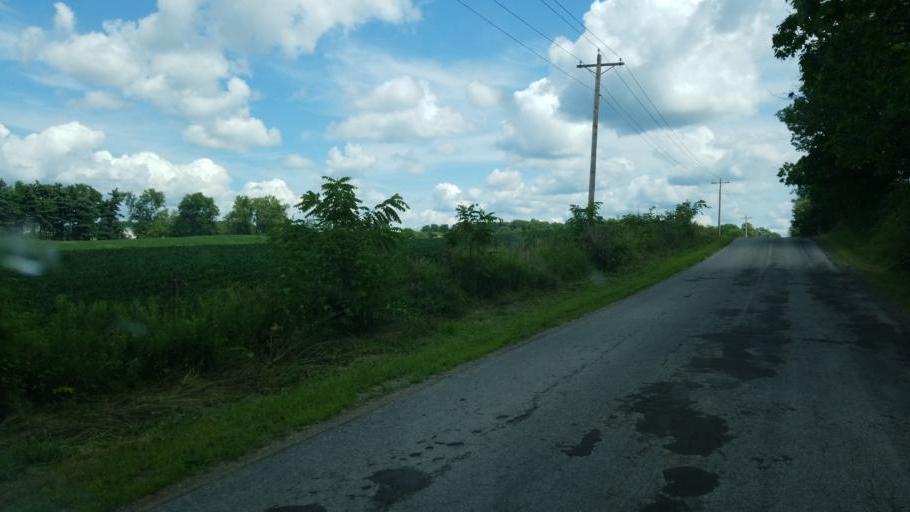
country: US
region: Ohio
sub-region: Knox County
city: Centerburg
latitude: 40.3644
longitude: -82.7361
